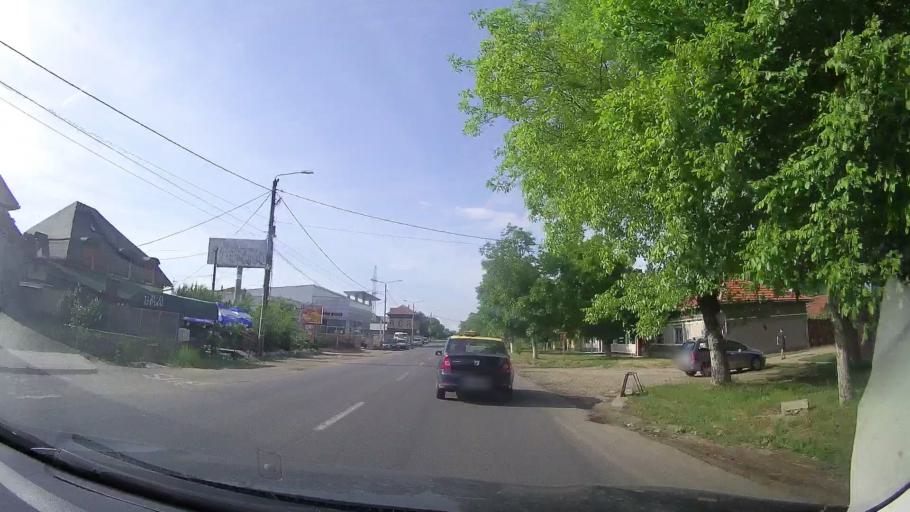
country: RO
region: Caras-Severin
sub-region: Municipiul Caransebes
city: Caransebes
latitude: 45.3929
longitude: 22.2272
